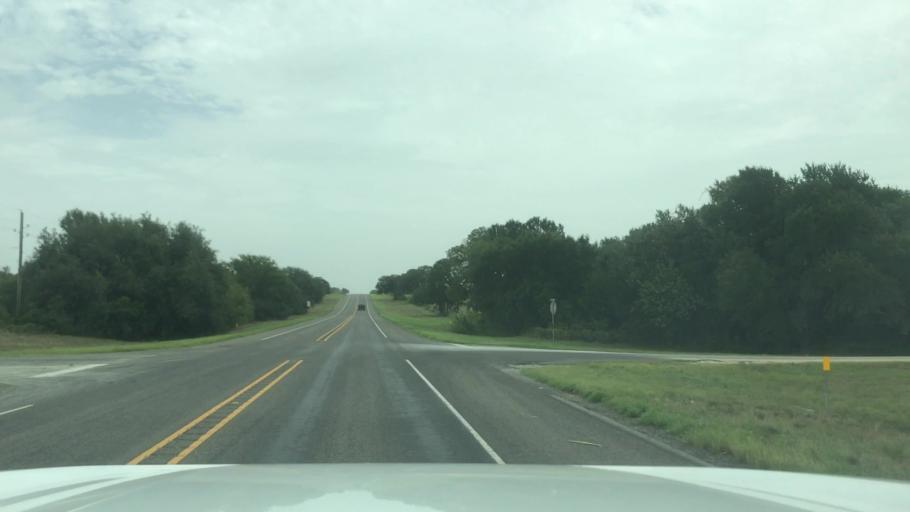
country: US
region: Texas
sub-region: Hamilton County
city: Hico
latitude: 31.9814
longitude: -98.0072
